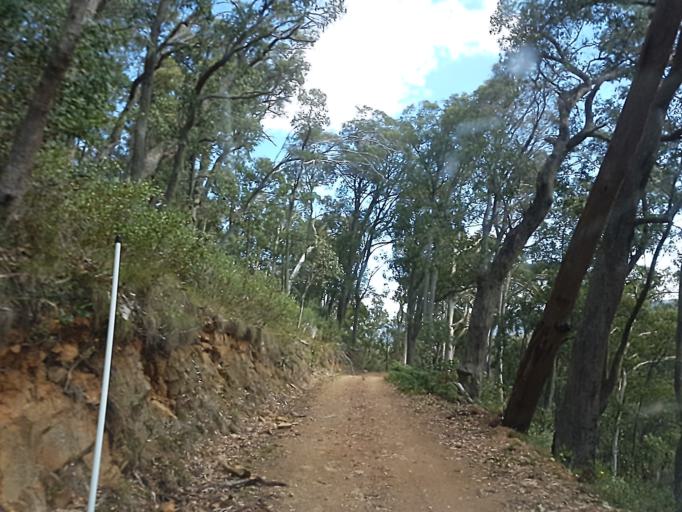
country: AU
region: Victoria
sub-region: Alpine
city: Mount Beauty
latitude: -36.9125
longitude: 147.0011
